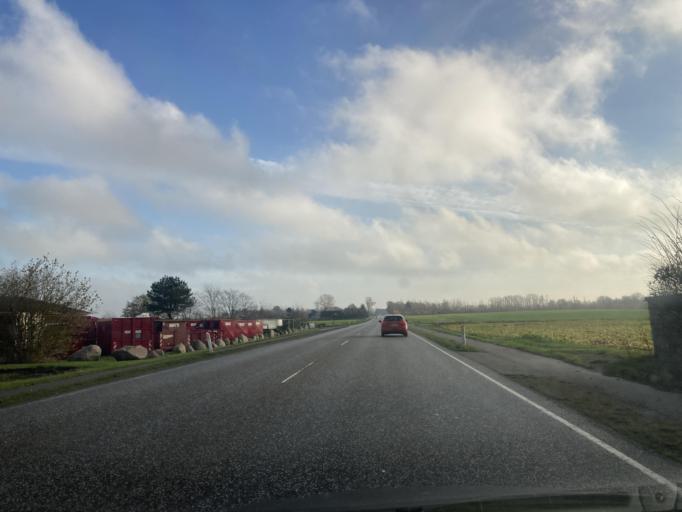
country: DK
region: Zealand
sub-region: Guldborgsund Kommune
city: Sundby
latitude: 54.7732
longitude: 11.7413
